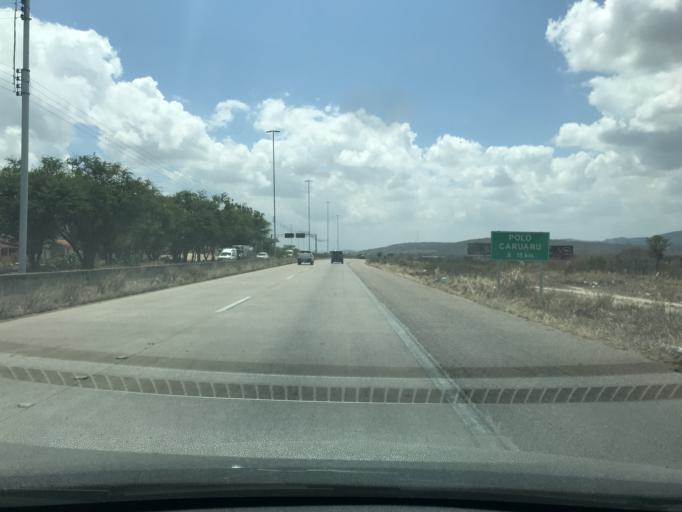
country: BR
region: Pernambuco
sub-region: Bezerros
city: Bezerros
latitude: -8.2999
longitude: -35.8514
